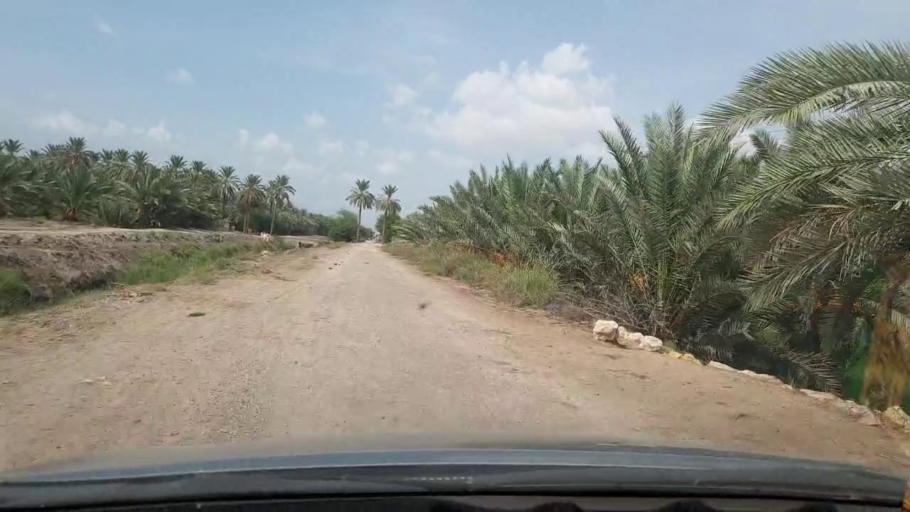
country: PK
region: Sindh
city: Khairpur
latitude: 27.5203
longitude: 68.8833
